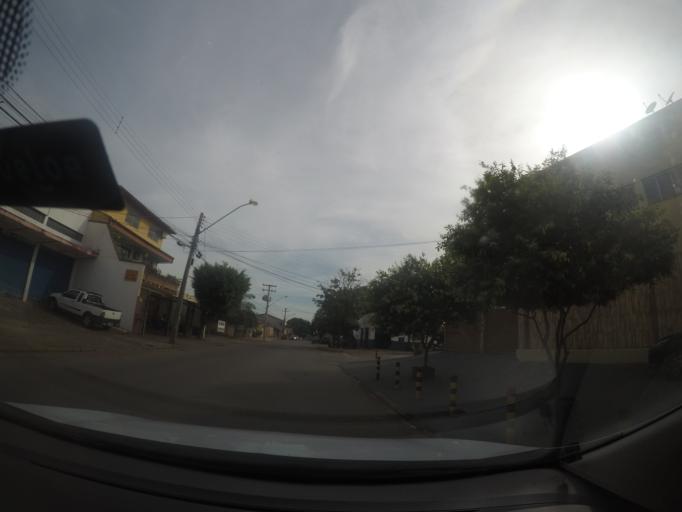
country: BR
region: Goias
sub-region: Goiania
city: Goiania
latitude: -16.6635
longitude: -49.3108
